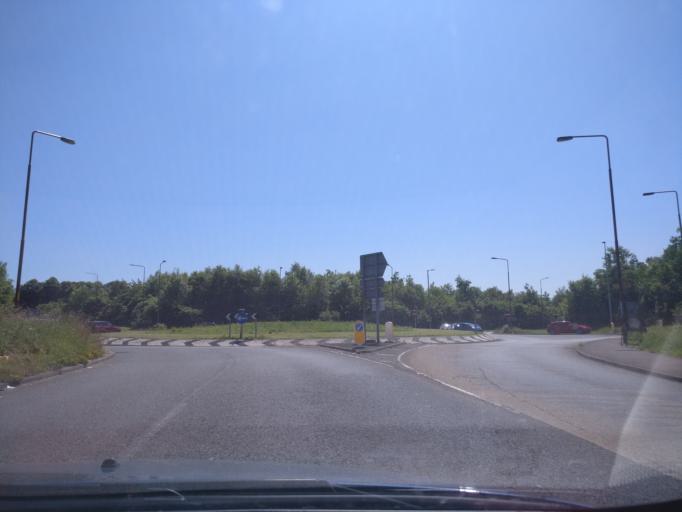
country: GB
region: Scotland
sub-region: East Lothian
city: Tranent
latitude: 55.9540
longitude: -2.9508
